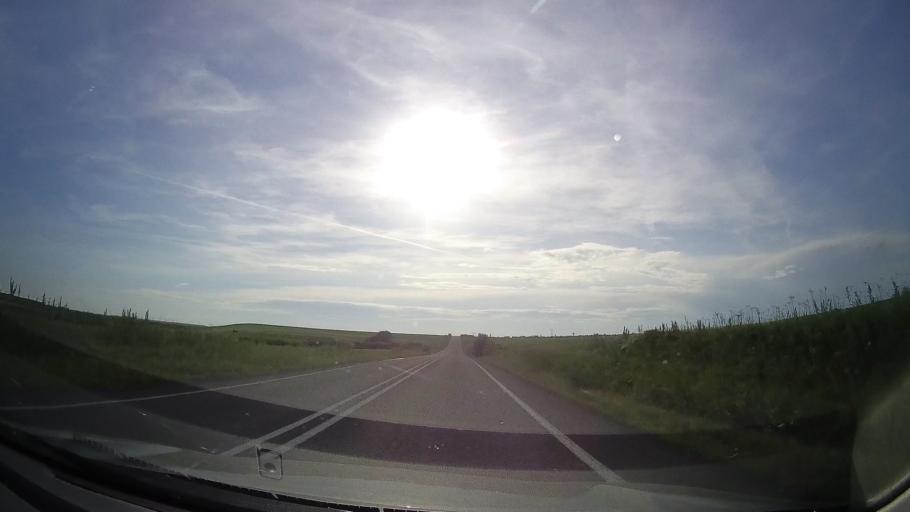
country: RO
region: Timis
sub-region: Oras Recas
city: Recas
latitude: 45.7946
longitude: 21.5455
